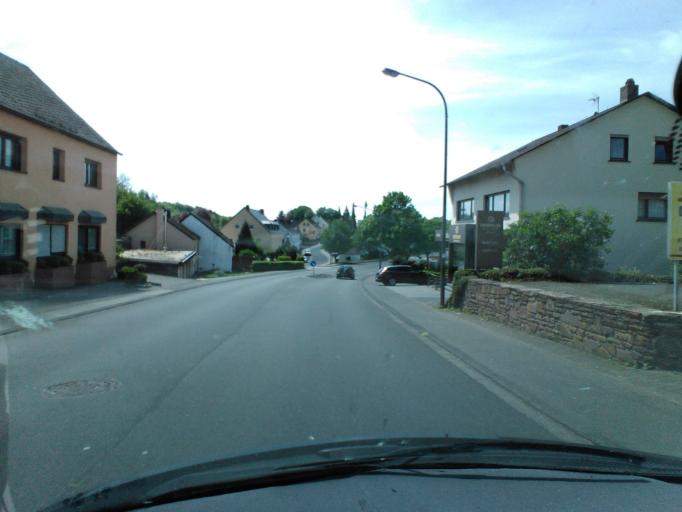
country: DE
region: Rheinland-Pfalz
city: Arzfeld
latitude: 50.0904
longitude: 6.2768
